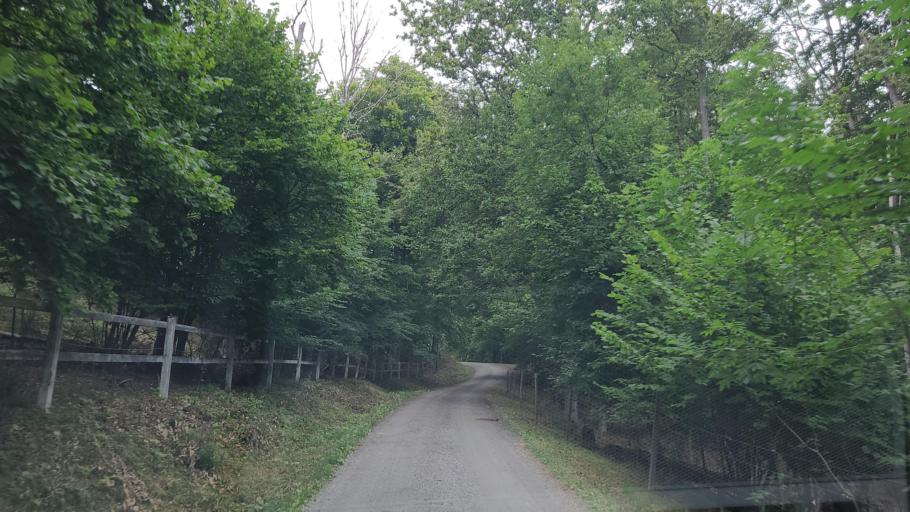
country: SE
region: Stockholm
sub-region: Upplands-Bro Kommun
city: Bro
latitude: 59.4550
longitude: 17.5820
